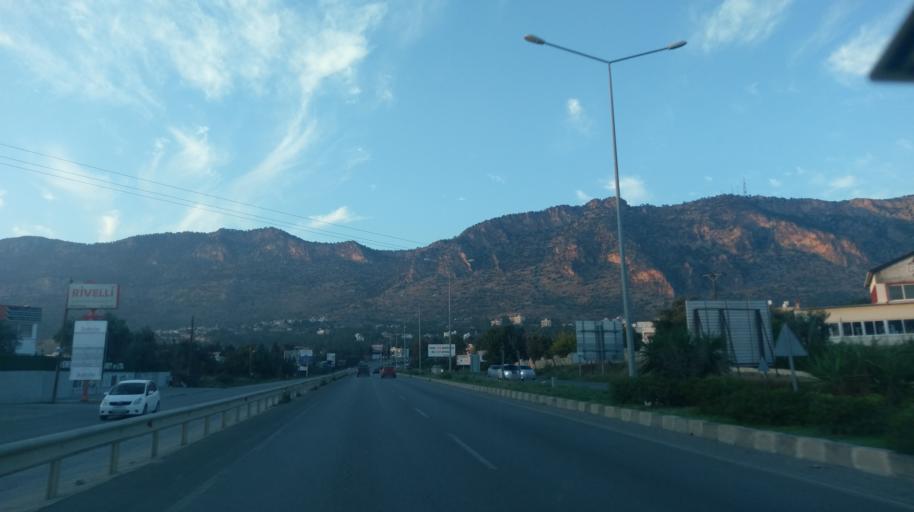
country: CY
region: Keryneia
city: Kyrenia
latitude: 35.2863
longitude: 33.2786
